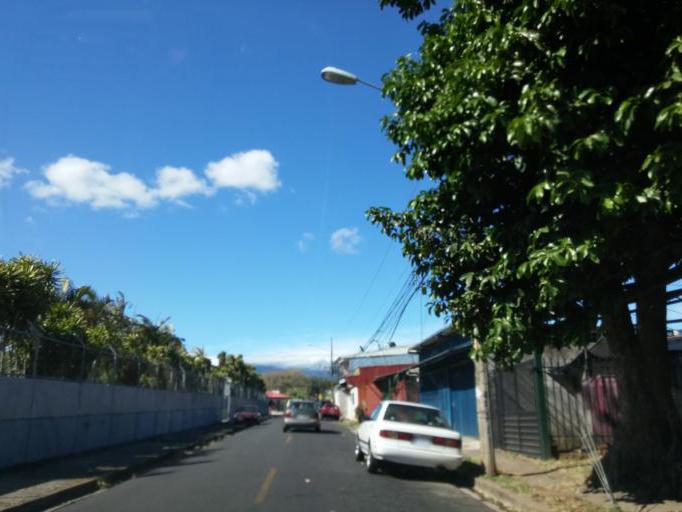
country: CR
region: Alajuela
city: Alajuela
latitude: 10.0170
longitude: -84.2036
